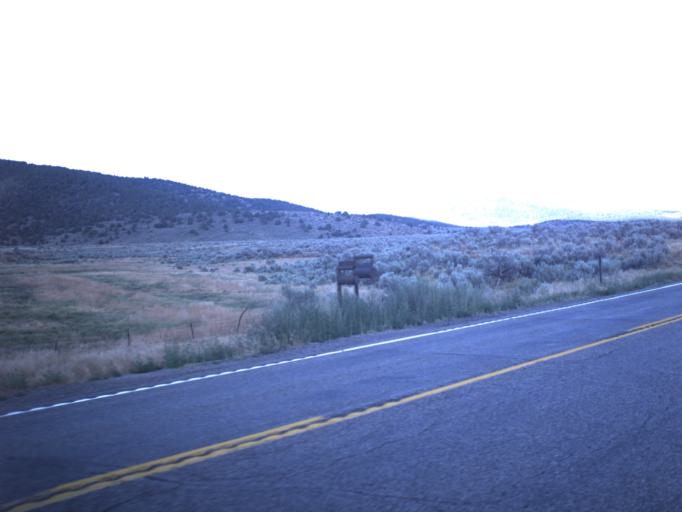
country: US
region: Utah
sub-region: Utah County
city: Woodland Hills
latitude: 39.8594
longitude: -111.5262
